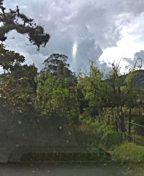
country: CO
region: Boyaca
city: Duitama
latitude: 5.8241
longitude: -73.0813
